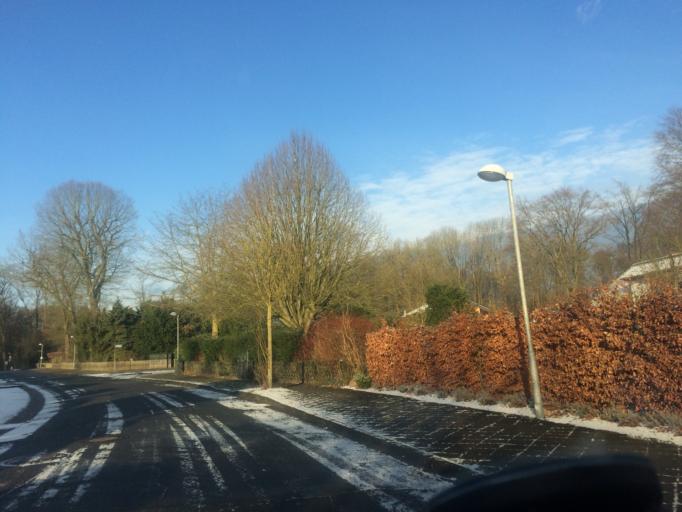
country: DE
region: Lower Saxony
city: Lueneburg
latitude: 53.2321
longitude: 10.4173
